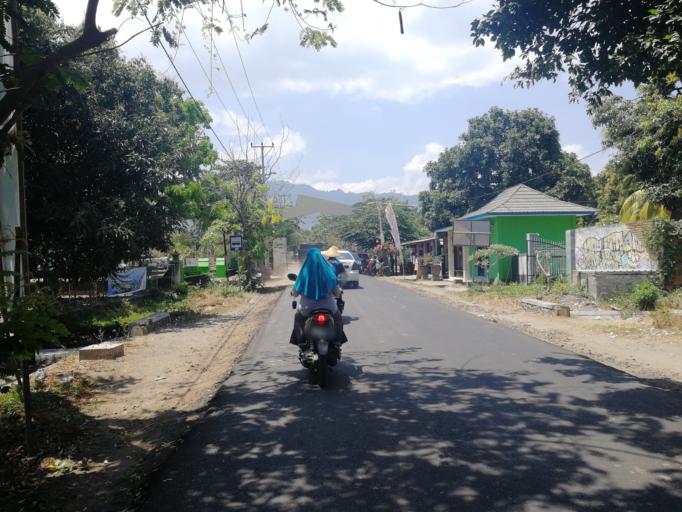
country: ID
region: West Nusa Tenggara
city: Pemenang
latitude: -8.3976
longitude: 116.1006
